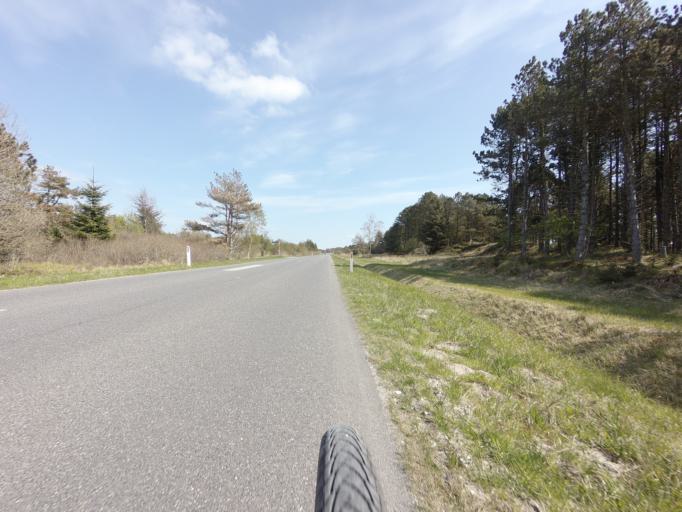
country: DK
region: North Denmark
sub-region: Jammerbugt Kommune
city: Brovst
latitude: 57.2017
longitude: 9.5440
